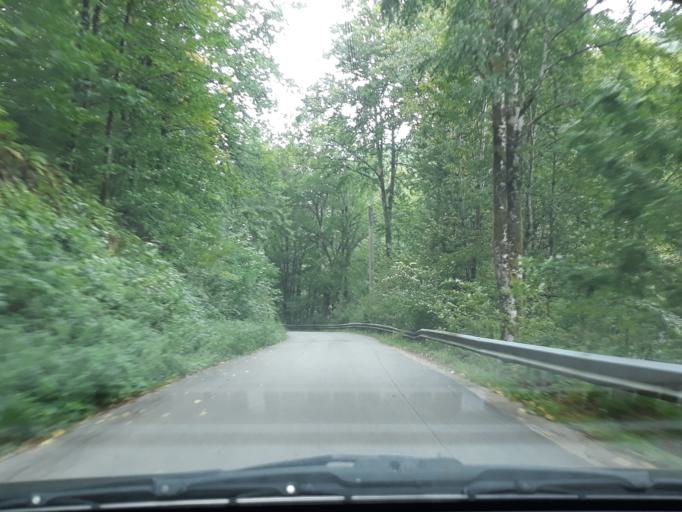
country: RO
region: Bihor
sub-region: Comuna Pietroasa
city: Pietroasa
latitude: 46.5878
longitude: 22.6185
